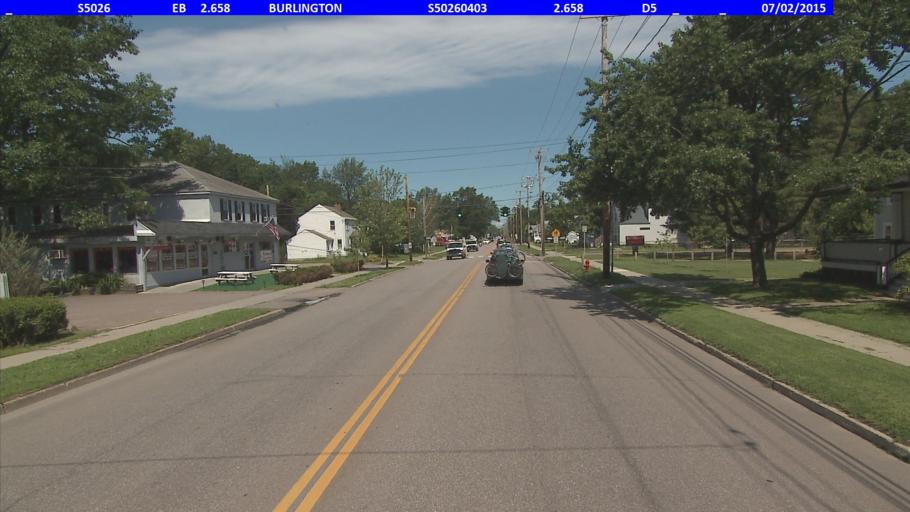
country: US
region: Vermont
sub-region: Chittenden County
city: Burlington
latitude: 44.5113
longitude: -73.2508
